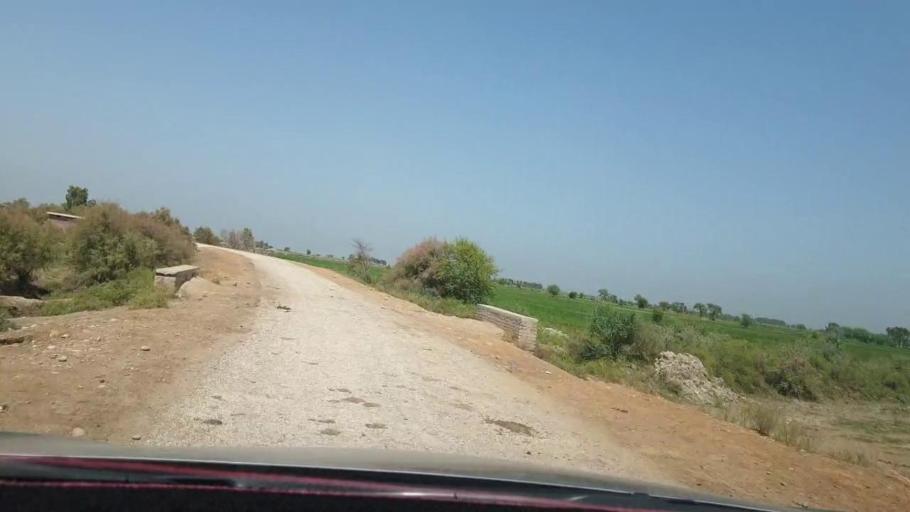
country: PK
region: Sindh
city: Warah
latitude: 27.5173
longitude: 67.7082
